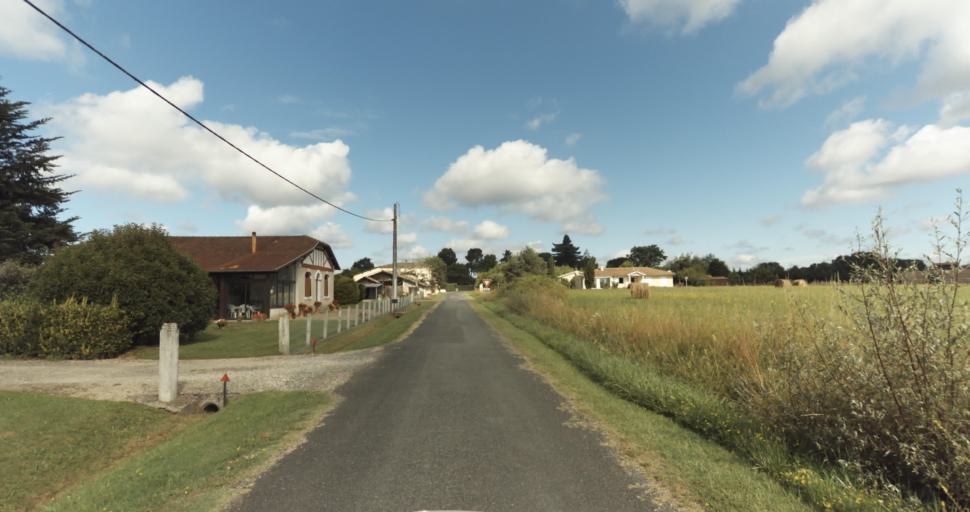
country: FR
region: Aquitaine
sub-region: Departement de la Gironde
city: Bazas
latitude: 44.4377
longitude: -0.2009
